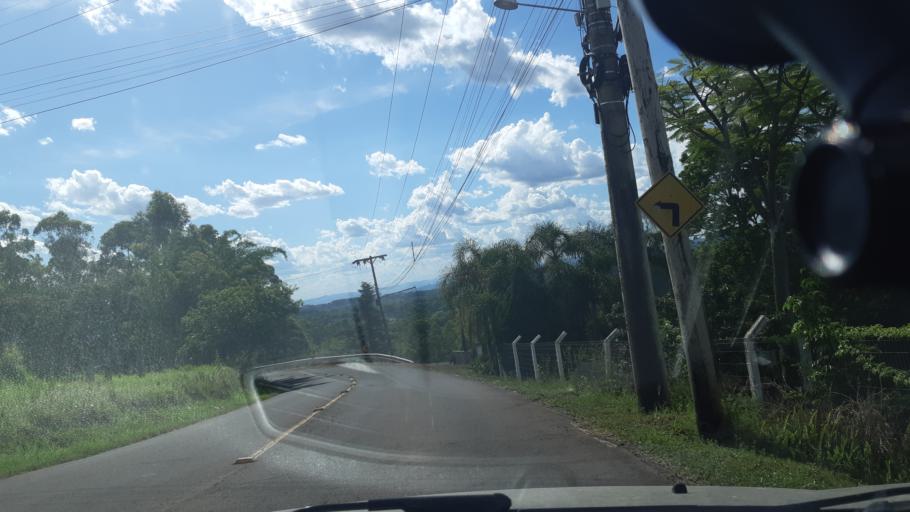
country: BR
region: Rio Grande do Sul
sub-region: Novo Hamburgo
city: Novo Hamburgo
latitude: -29.6259
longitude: -51.1033
